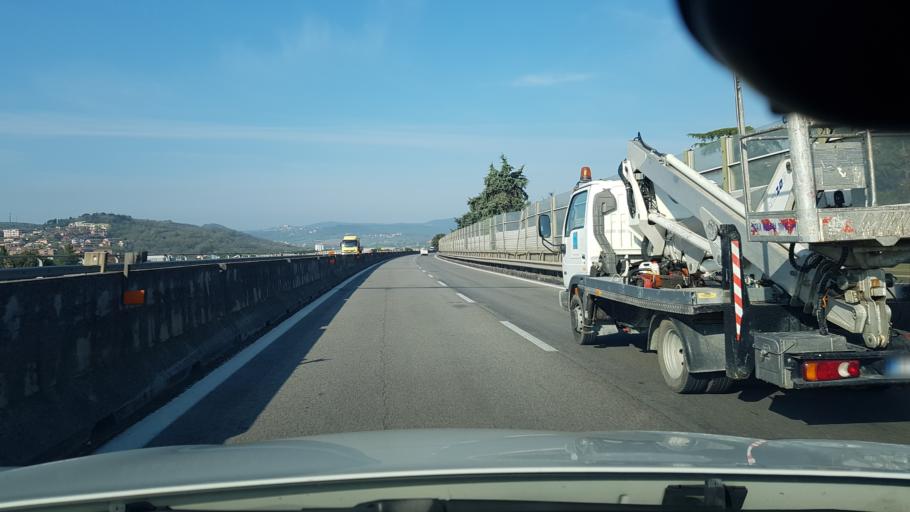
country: IT
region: Umbria
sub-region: Provincia di Perugia
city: Chiugiana-La Commenda
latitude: 43.1032
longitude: 12.3203
